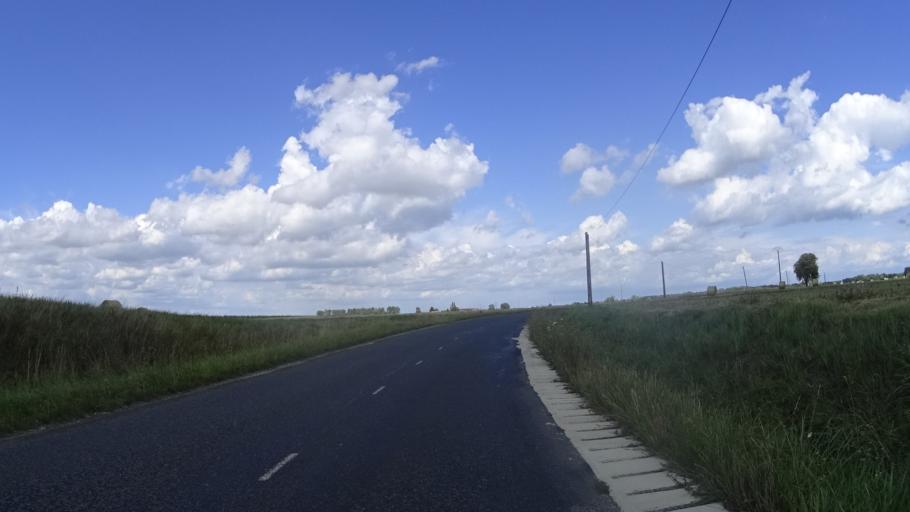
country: FR
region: Champagne-Ardenne
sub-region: Departement de la Marne
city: Pargny-sur-Saulx
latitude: 48.7375
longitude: 4.7794
